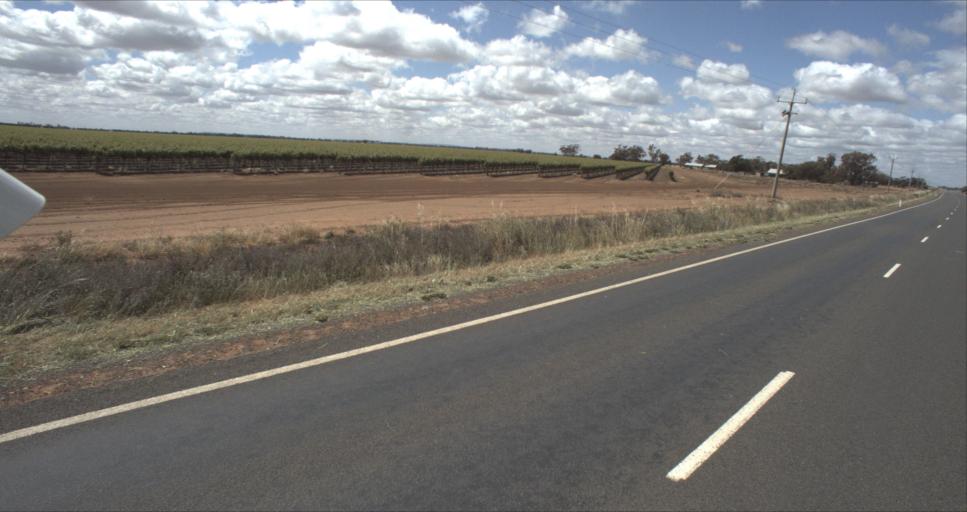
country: AU
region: New South Wales
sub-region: Murrumbidgee Shire
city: Darlington Point
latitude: -34.4771
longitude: 146.1503
